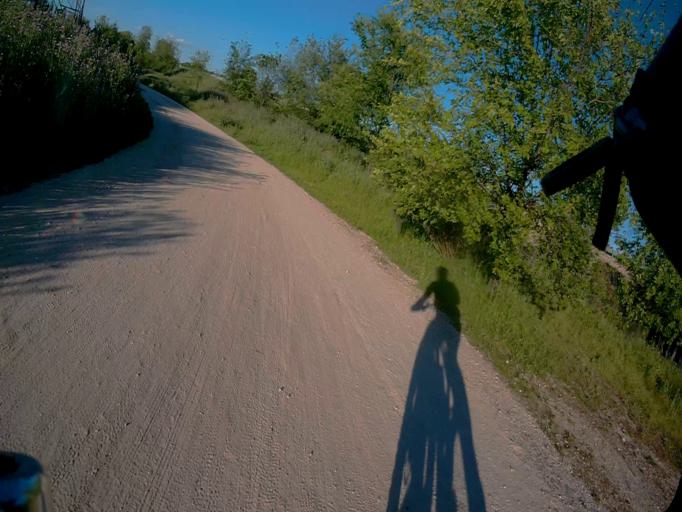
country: ES
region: Madrid
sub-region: Provincia de Madrid
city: Fuenlabrada
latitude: 40.3154
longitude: -3.7956
